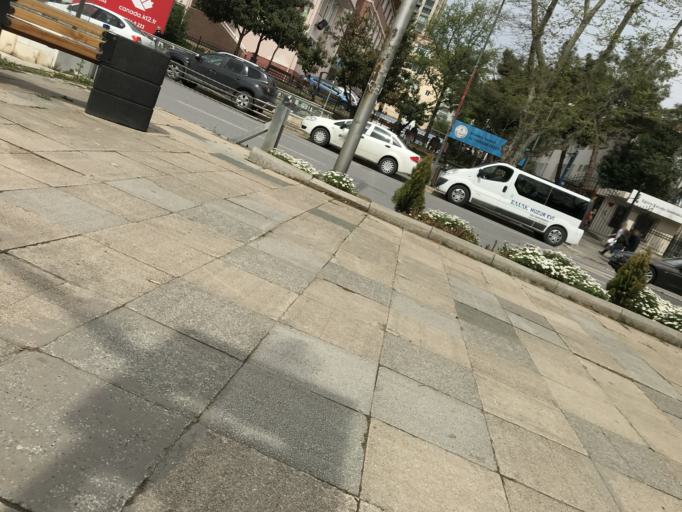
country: TR
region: Istanbul
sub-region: Atasehir
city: Atasehir
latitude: 40.9724
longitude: 29.0577
